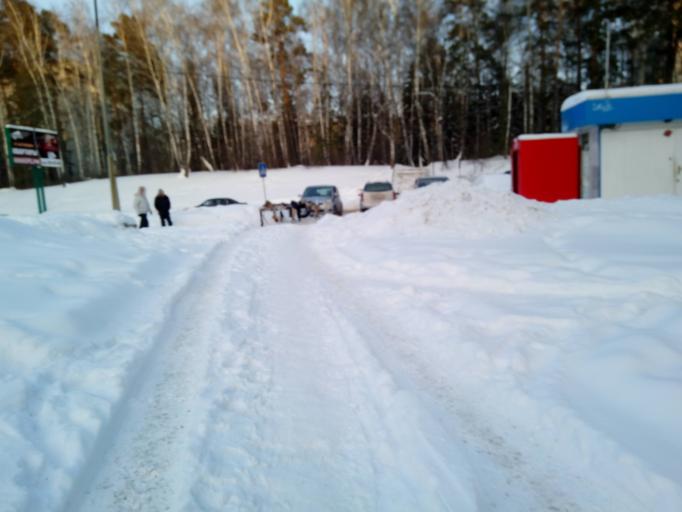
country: RU
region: Novosibirsk
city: Akademgorodok
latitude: 54.8379
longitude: 83.0976
